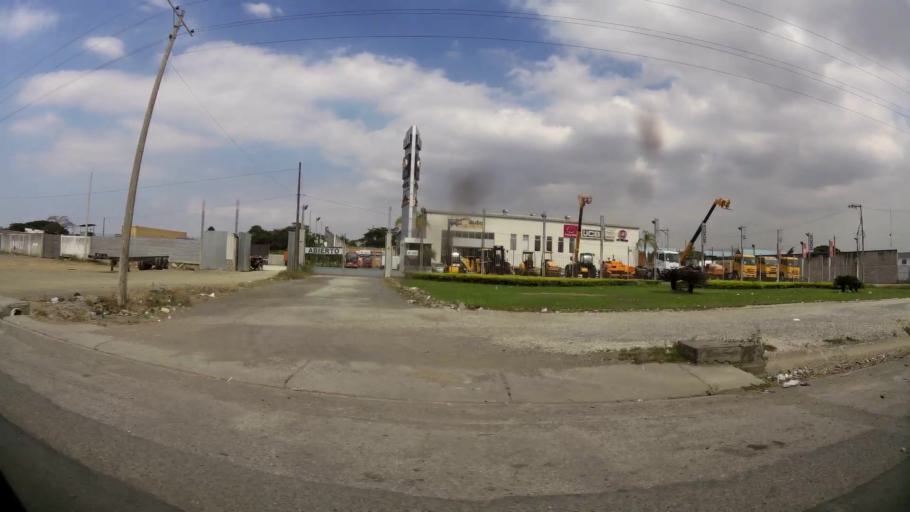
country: EC
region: Guayas
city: Santa Lucia
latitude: -2.0846
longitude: -79.9436
